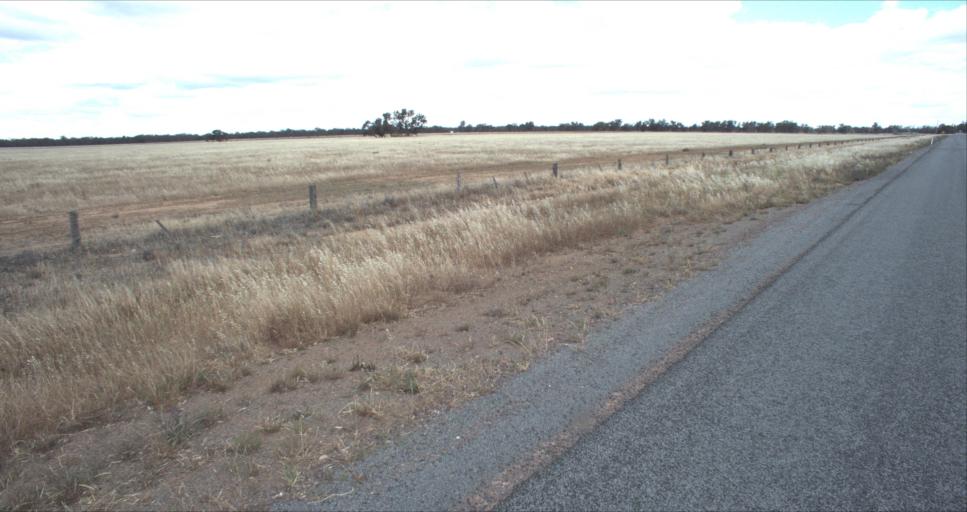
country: AU
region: New South Wales
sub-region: Leeton
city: Leeton
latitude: -34.6932
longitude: 146.3433
